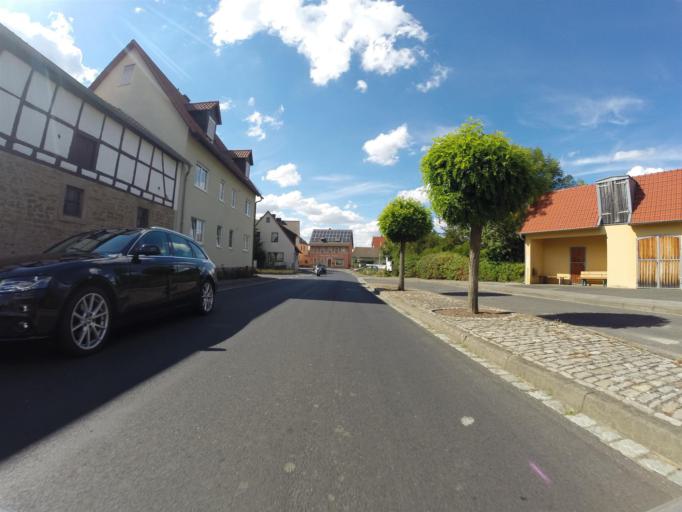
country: DE
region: Bavaria
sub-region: Regierungsbezirk Unterfranken
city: Donnersdorf
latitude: 49.9397
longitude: 10.4121
